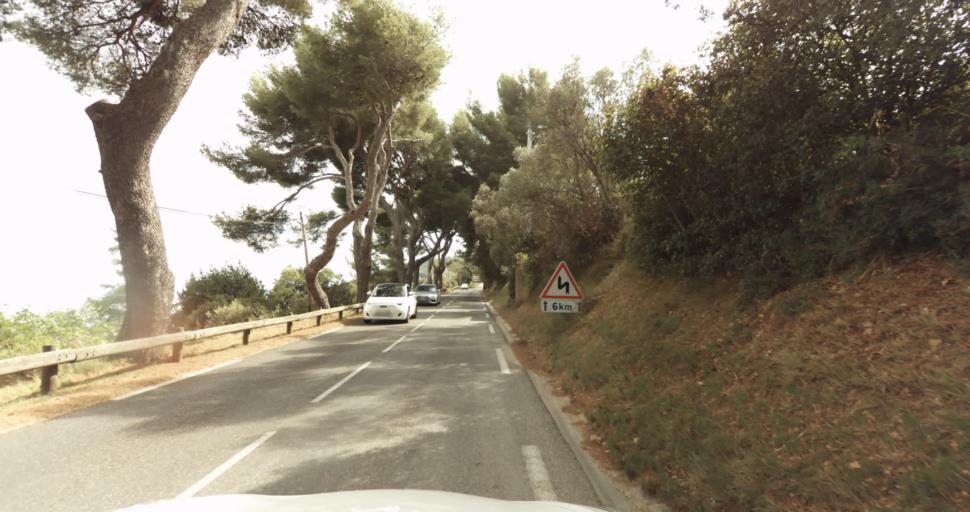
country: FR
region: Provence-Alpes-Cote d'Azur
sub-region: Departement des Bouches-du-Rhone
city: Saint-Chamas
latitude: 43.5537
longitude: 5.0121
